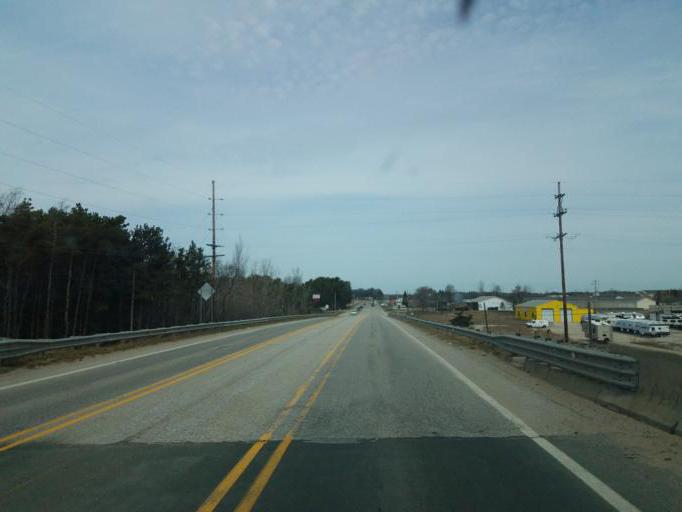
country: US
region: Michigan
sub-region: Mason County
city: Ludington
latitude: 43.9502
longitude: -86.4157
